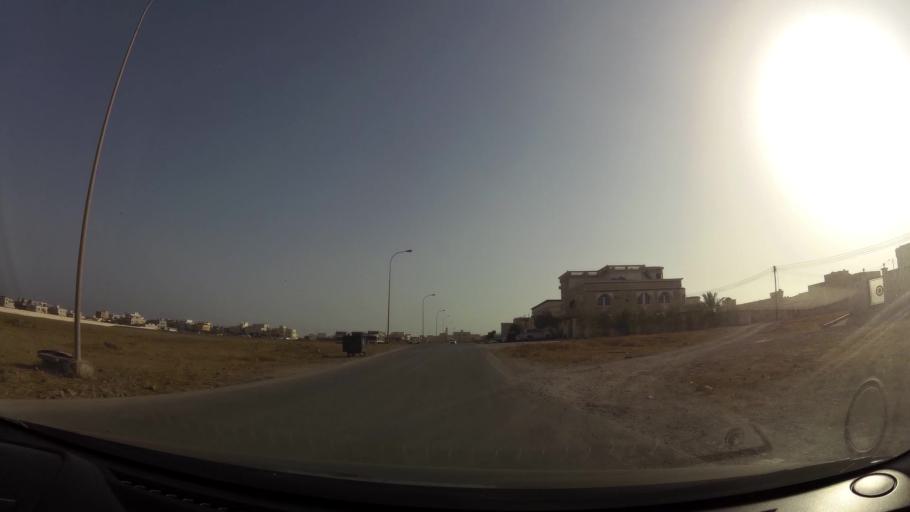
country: OM
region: Zufar
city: Salalah
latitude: 17.0183
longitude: 54.0234
